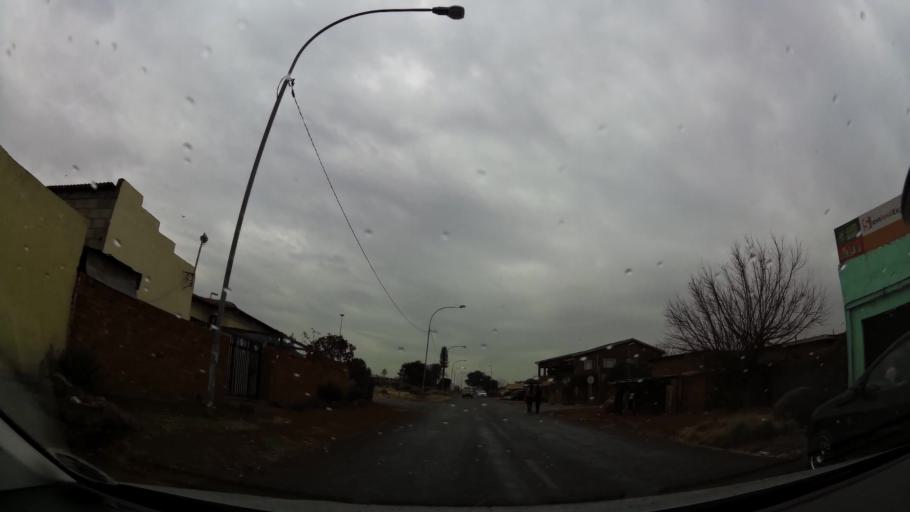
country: ZA
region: Gauteng
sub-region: City of Johannesburg Metropolitan Municipality
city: Soweto
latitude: -26.2491
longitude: 27.8672
